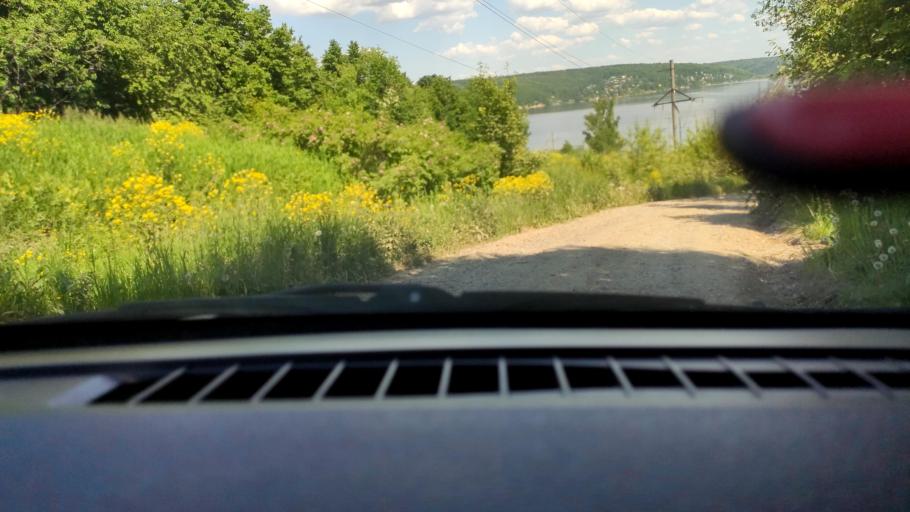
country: RU
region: Perm
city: Sylva
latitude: 58.0370
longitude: 56.7803
